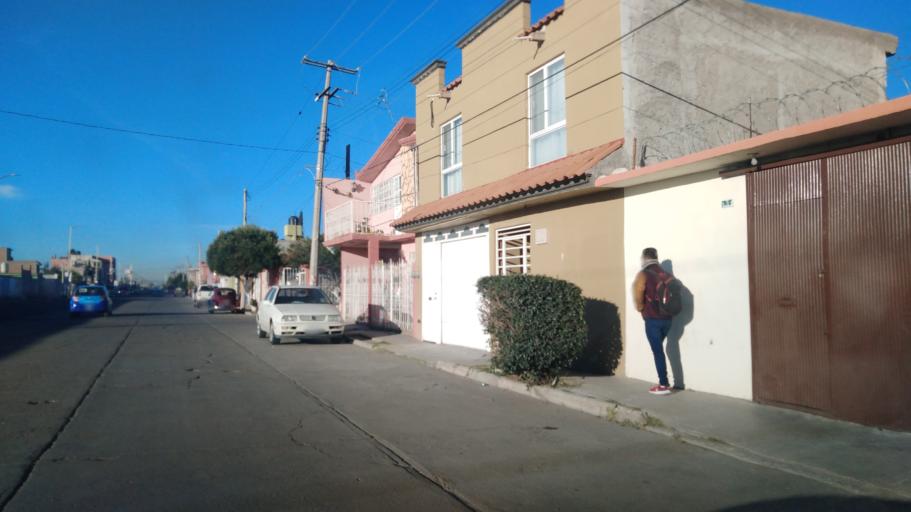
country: MX
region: Durango
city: Victoria de Durango
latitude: 24.0547
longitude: -104.6041
